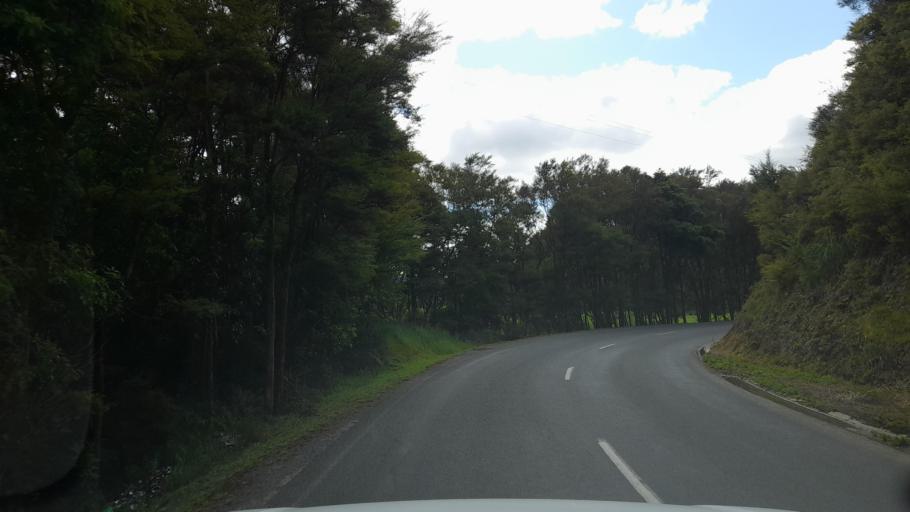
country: NZ
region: Northland
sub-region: Whangarei
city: Maungatapere
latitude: -35.6703
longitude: 174.0399
